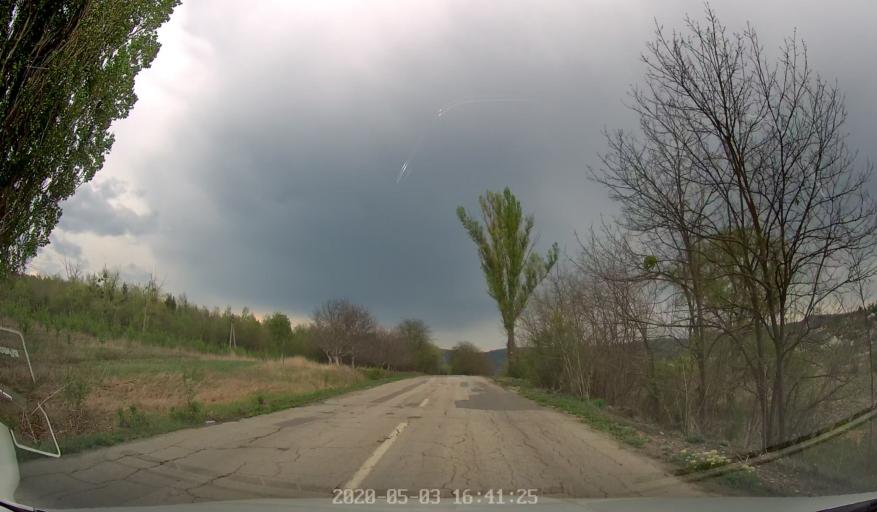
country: MD
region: Stinga Nistrului
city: Bucovat
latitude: 47.1672
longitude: 28.4080
